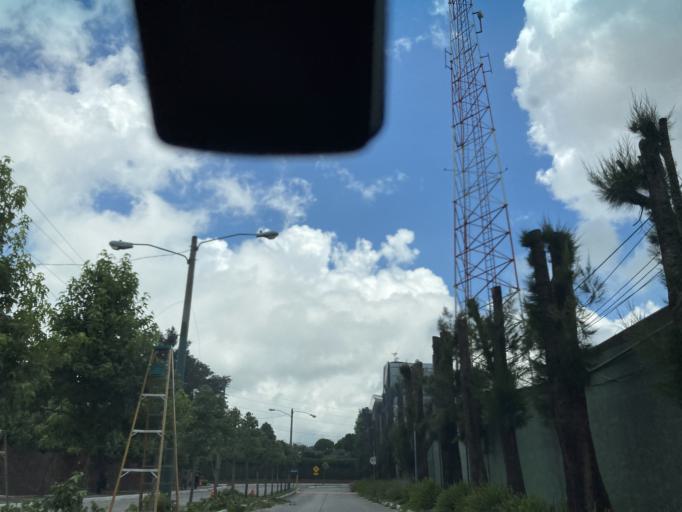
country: GT
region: Guatemala
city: San Jose Pinula
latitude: 14.5433
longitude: -90.4284
